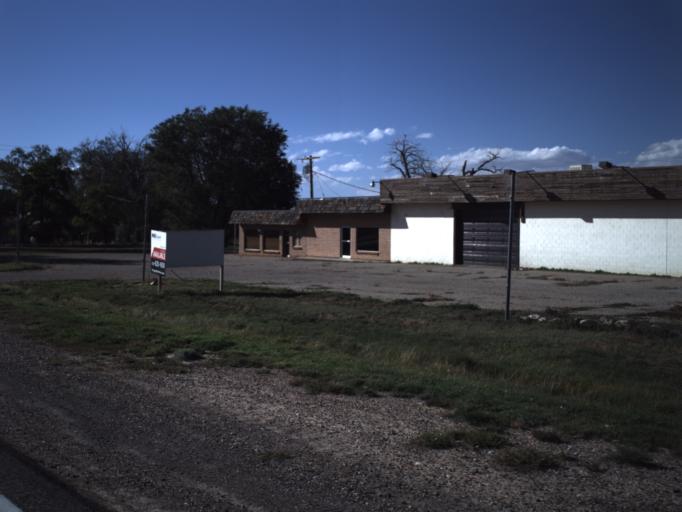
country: US
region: Utah
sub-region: Iron County
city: Parowan
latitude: 37.8386
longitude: -112.8564
